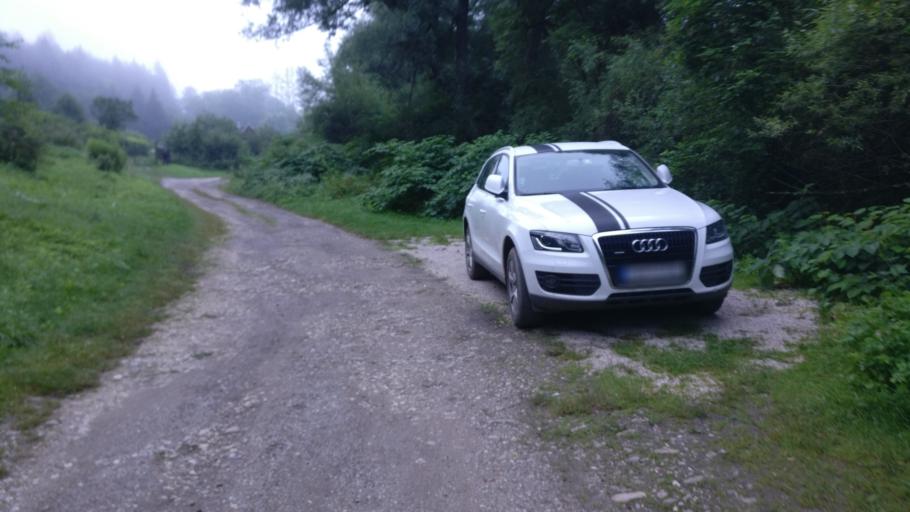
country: SK
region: Zilinsky
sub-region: Okres Zilina
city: Zilina
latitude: 49.2440
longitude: 18.7536
